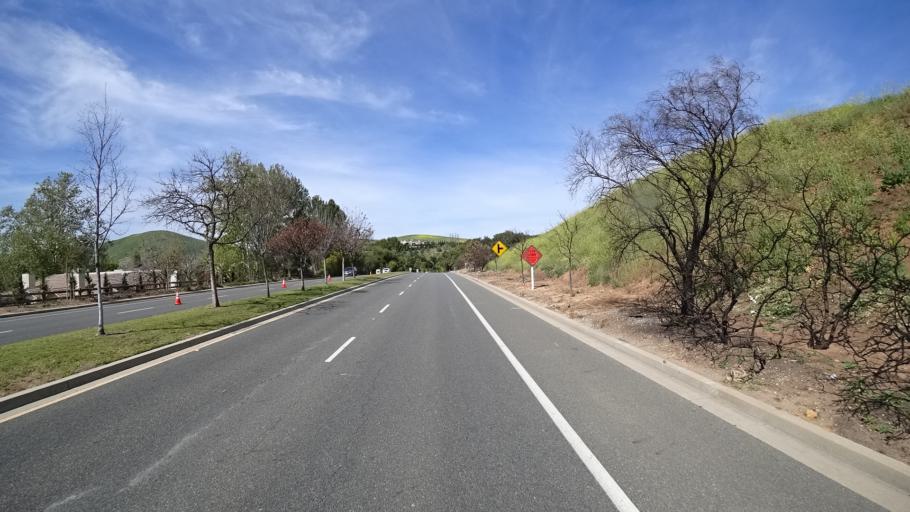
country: US
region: California
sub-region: Ventura County
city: Thousand Oaks
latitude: 34.1995
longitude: -118.8157
